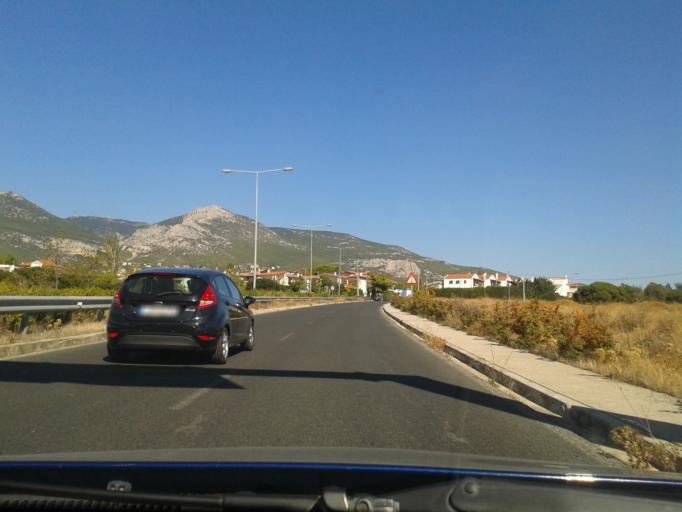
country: GR
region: Attica
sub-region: Nomarchia Anatolikis Attikis
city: Thrakomakedones
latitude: 38.1176
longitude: 23.7622
